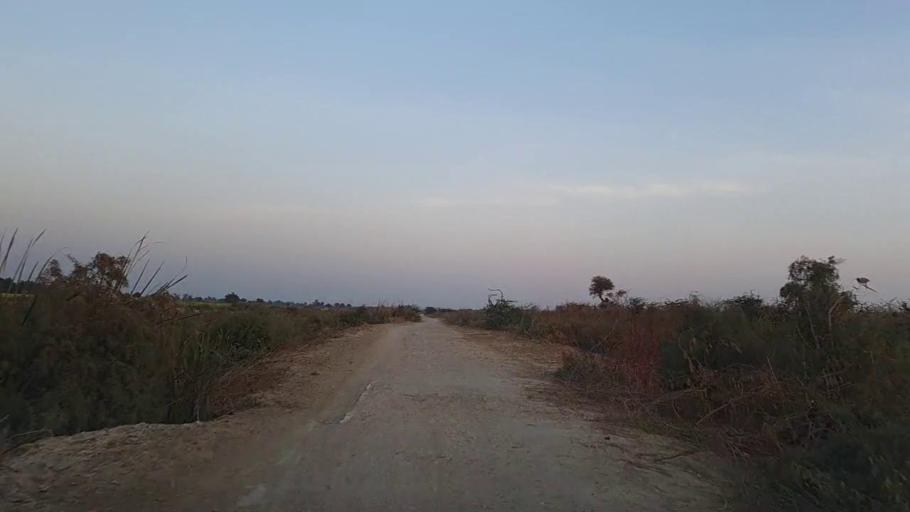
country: PK
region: Sindh
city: Tando Mittha Khan
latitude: 25.9455
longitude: 69.1241
